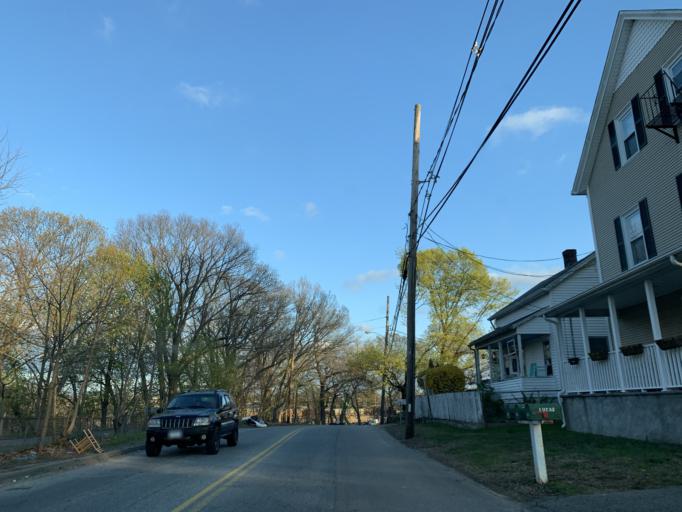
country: US
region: Rhode Island
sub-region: Providence County
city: Valley Falls
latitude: 41.8988
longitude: -71.3772
